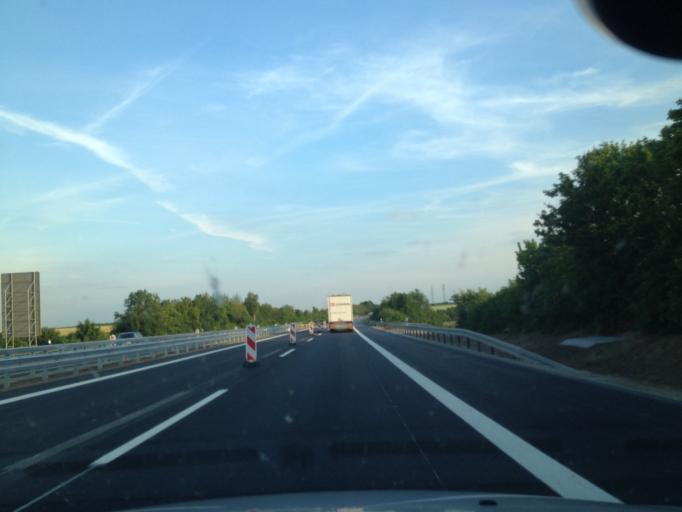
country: DE
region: Bavaria
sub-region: Regierungsbezirk Unterfranken
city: Biebelried
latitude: 49.7498
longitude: 10.1073
